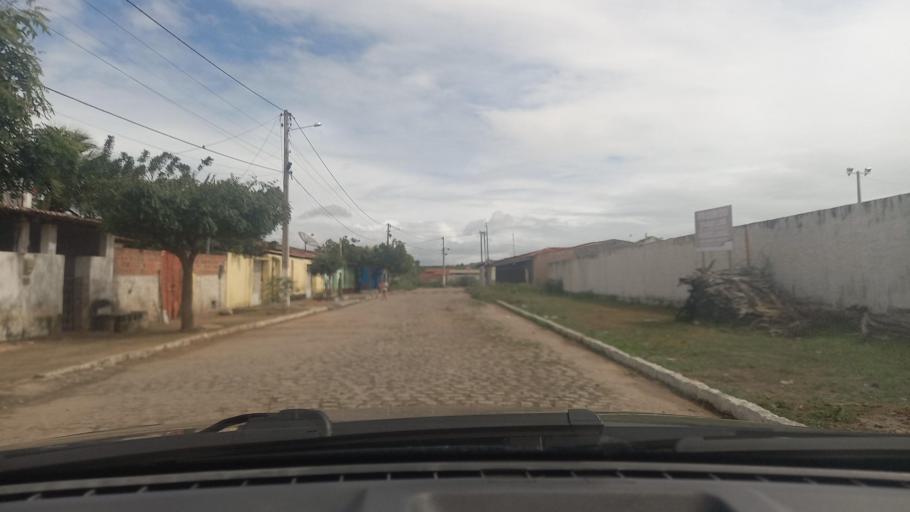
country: BR
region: Bahia
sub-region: Paulo Afonso
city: Paulo Afonso
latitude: -9.3465
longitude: -38.2597
